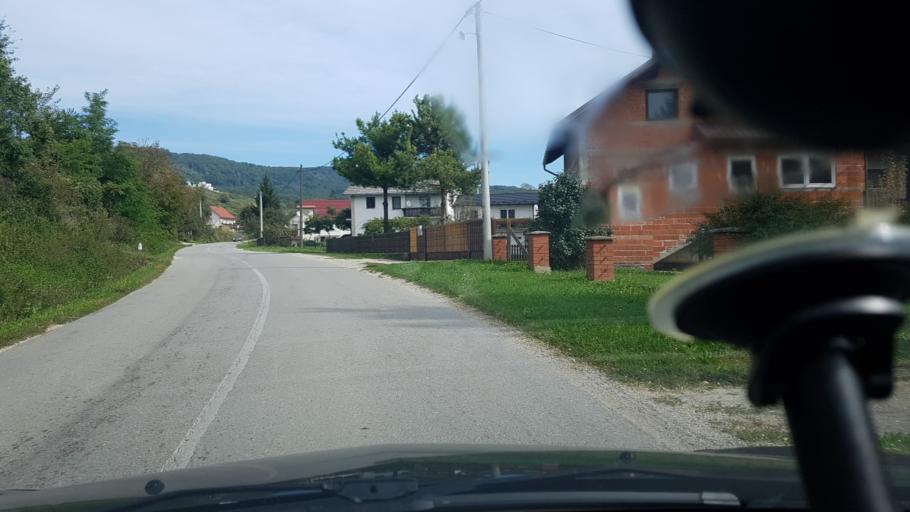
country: HR
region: Varazdinska
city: Ljubescica
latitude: 46.1034
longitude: 16.3609
